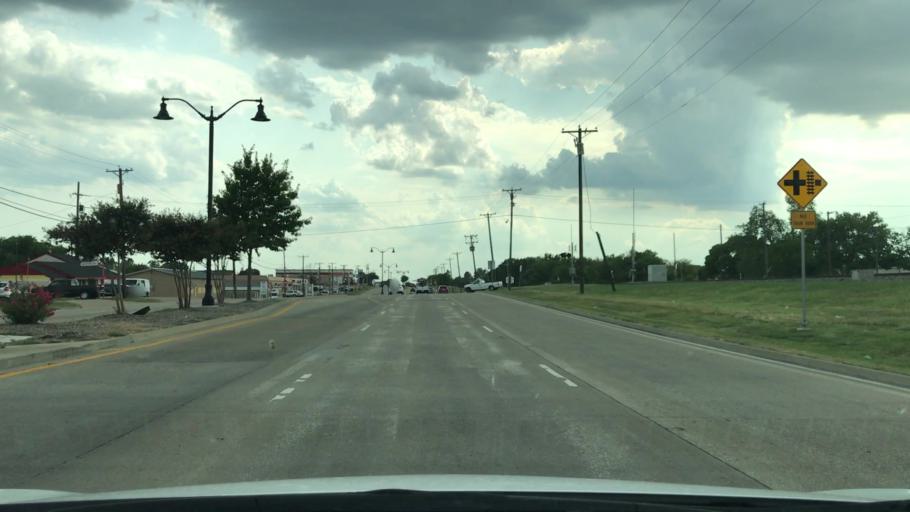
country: US
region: Texas
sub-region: Dallas County
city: Sachse
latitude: 32.9762
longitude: -96.5956
